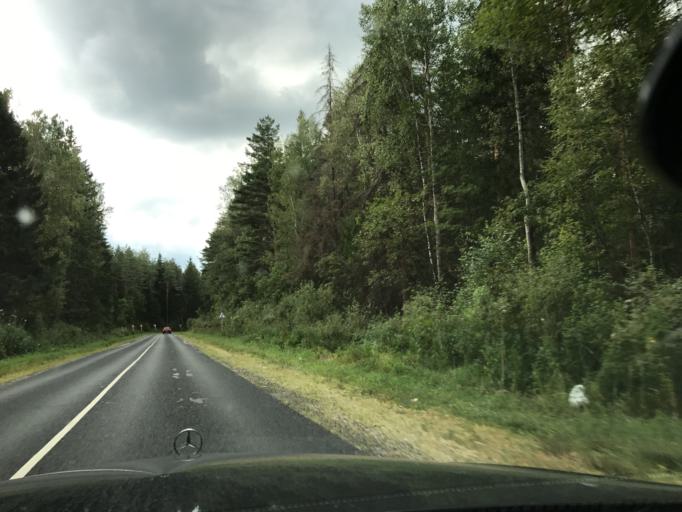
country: RU
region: Vladimir
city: Raduzhnyy
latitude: 55.9862
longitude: 40.2582
